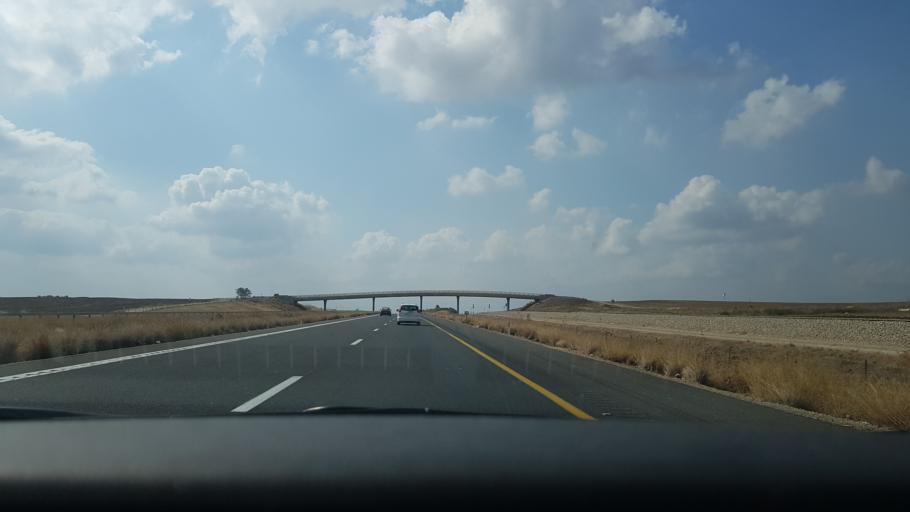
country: IL
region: Central District
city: Gedera
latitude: 31.7665
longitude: 34.8287
